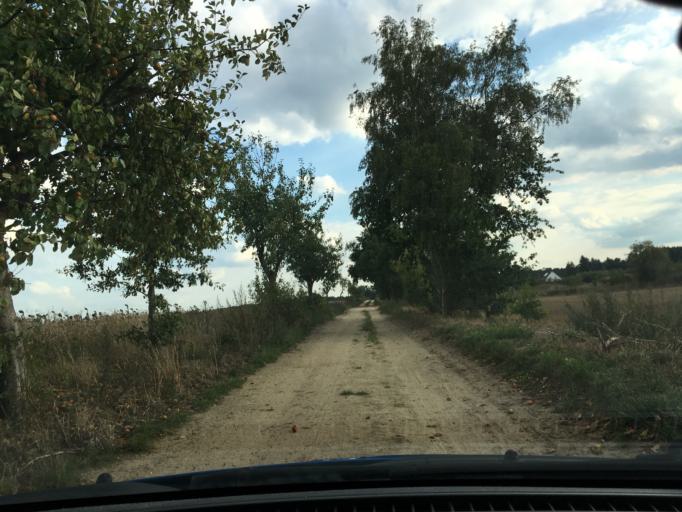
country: DE
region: Lower Saxony
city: Wulfsen
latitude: 53.2953
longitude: 10.1526
